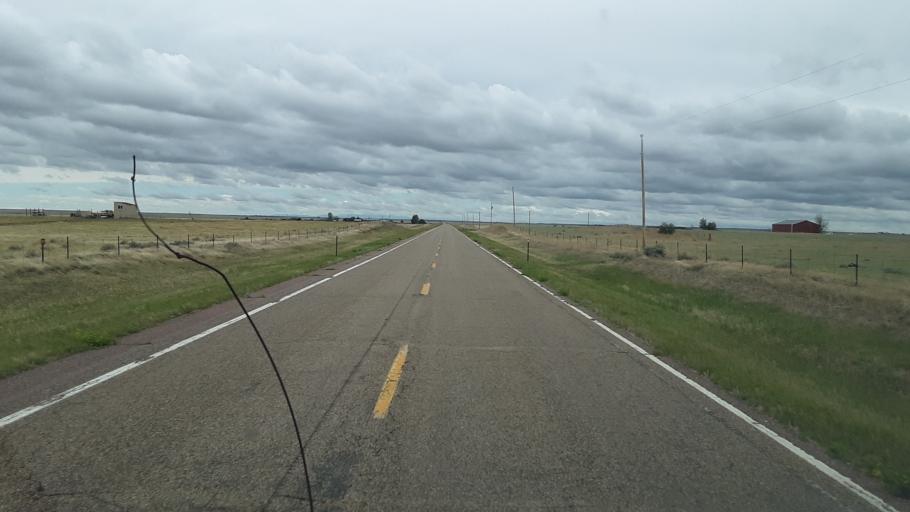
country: US
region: Colorado
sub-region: Lincoln County
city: Limon
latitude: 38.8387
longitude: -103.8796
